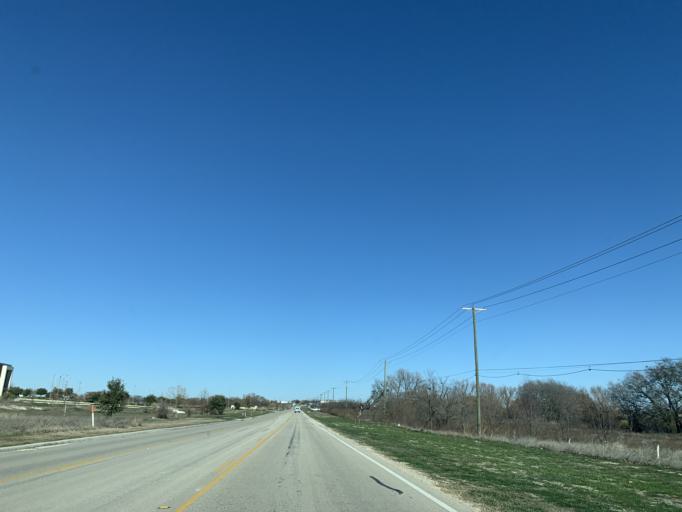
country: US
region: Texas
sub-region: Williamson County
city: Hutto
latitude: 30.5512
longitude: -97.5721
